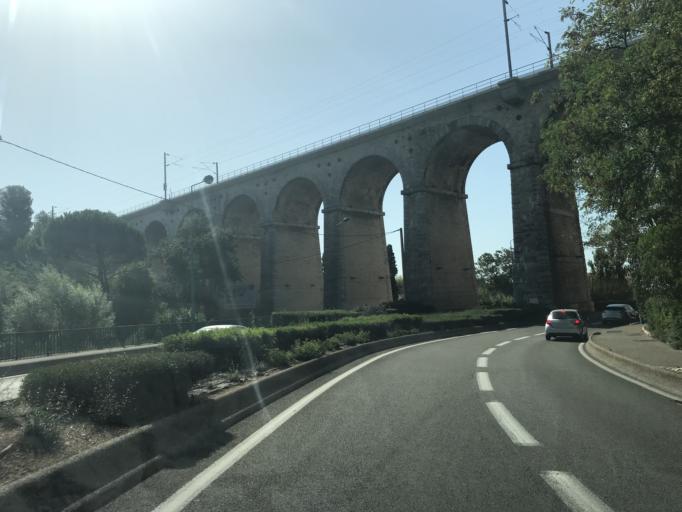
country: FR
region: Provence-Alpes-Cote d'Azur
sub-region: Departement du Var
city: Sanary-sur-Mer
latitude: 43.1410
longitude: 5.7714
